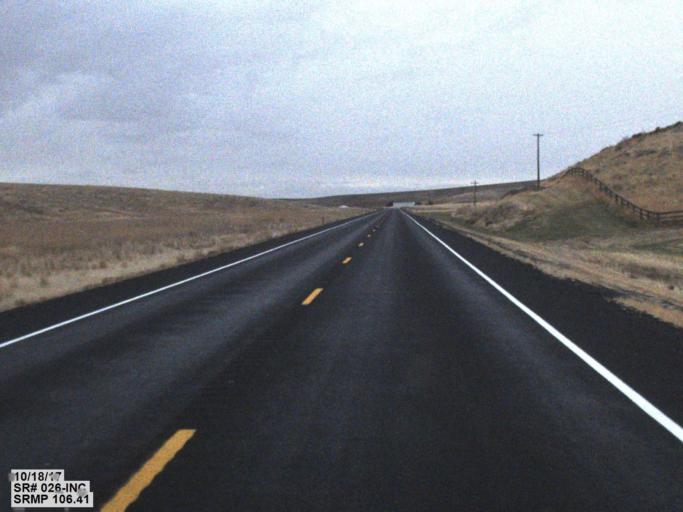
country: US
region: Washington
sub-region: Garfield County
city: Pomeroy
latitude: 46.7979
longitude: -117.8625
